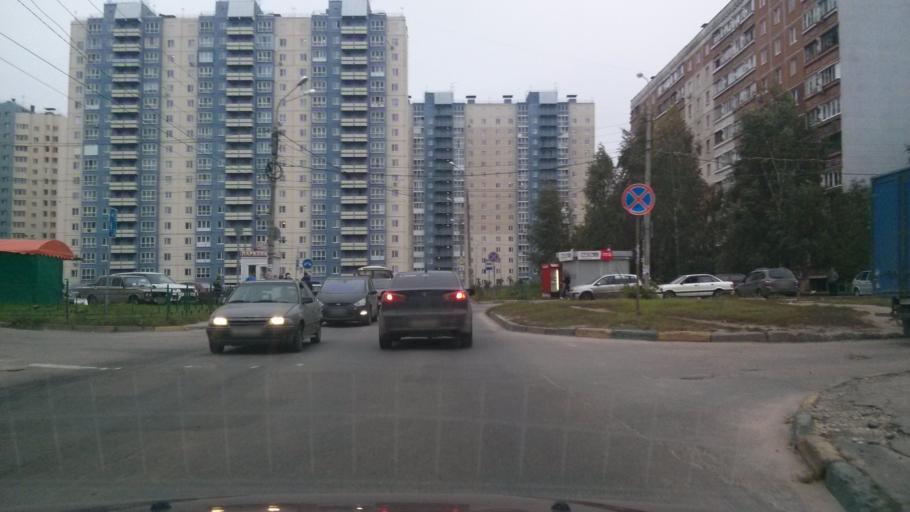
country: RU
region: Nizjnij Novgorod
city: Afonino
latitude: 56.2860
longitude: 44.0682
